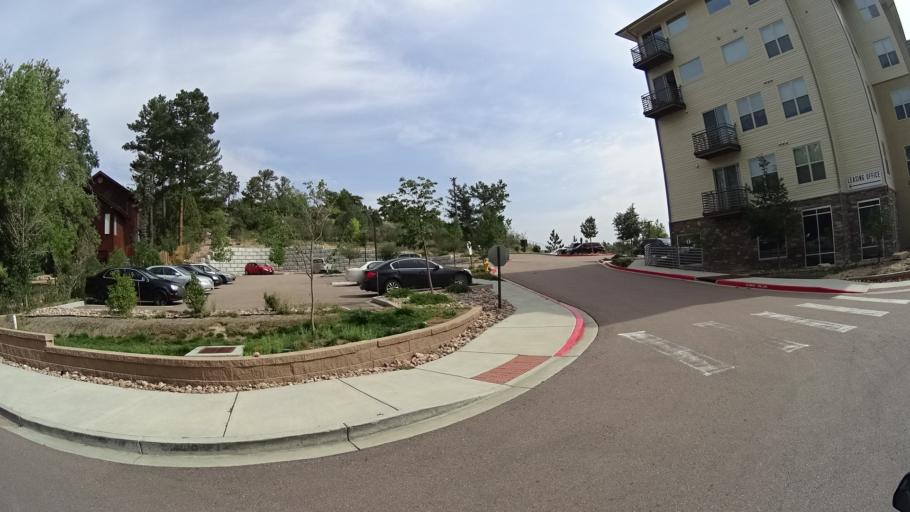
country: US
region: Colorado
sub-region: El Paso County
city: Colorado Springs
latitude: 38.8901
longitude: -104.7938
